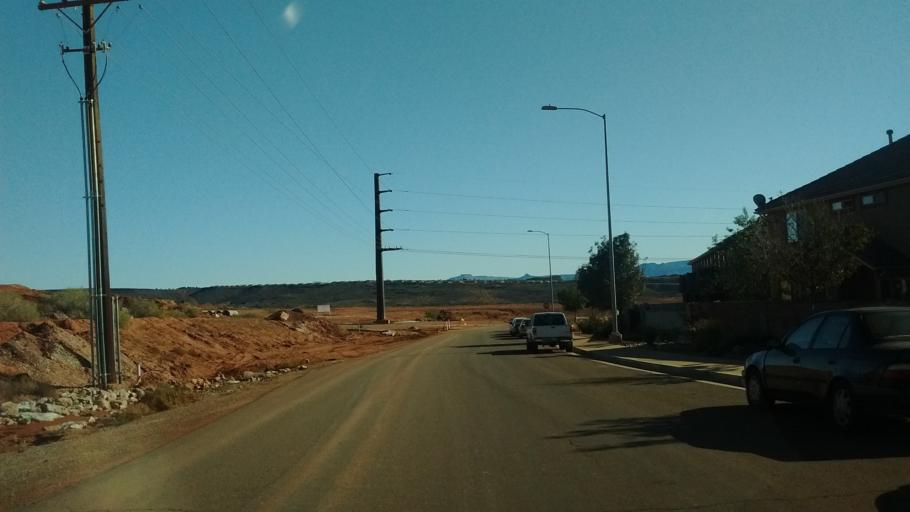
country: US
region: Utah
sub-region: Washington County
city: Washington
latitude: 37.1412
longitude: -113.4923
